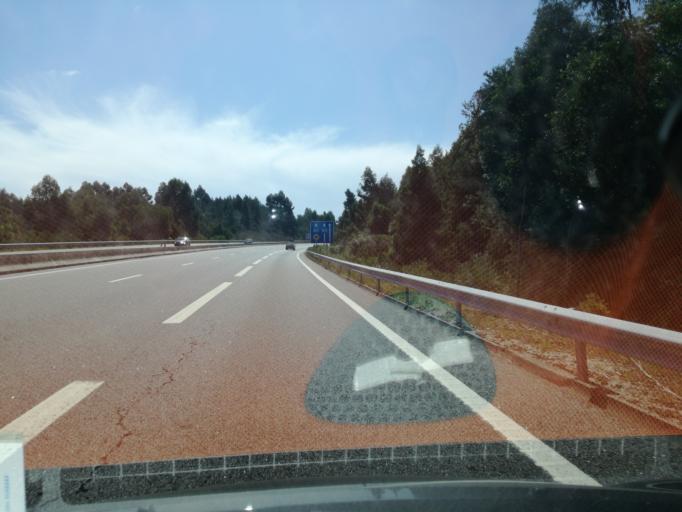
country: PT
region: Viana do Castelo
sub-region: Caminha
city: Vila Praia de Ancora
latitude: 41.7886
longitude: -8.7900
